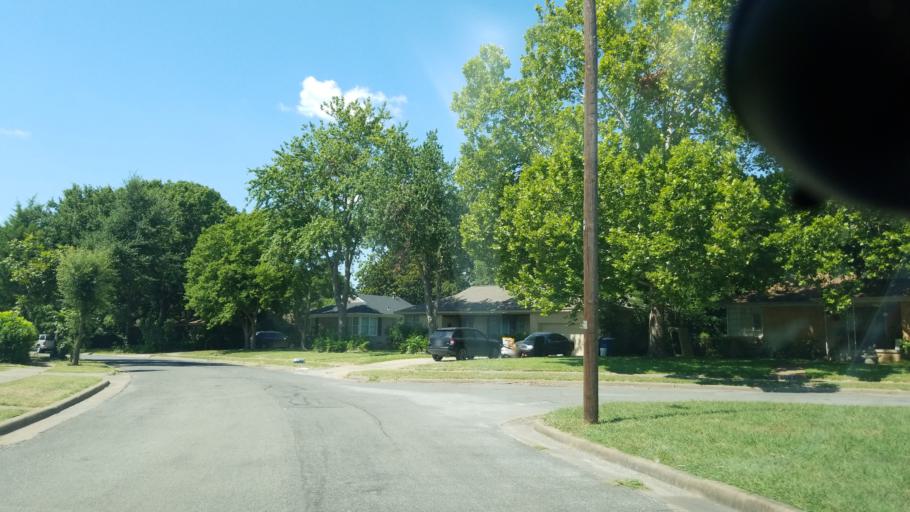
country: US
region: Texas
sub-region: Dallas County
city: Cockrell Hill
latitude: 32.7195
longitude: -96.8391
